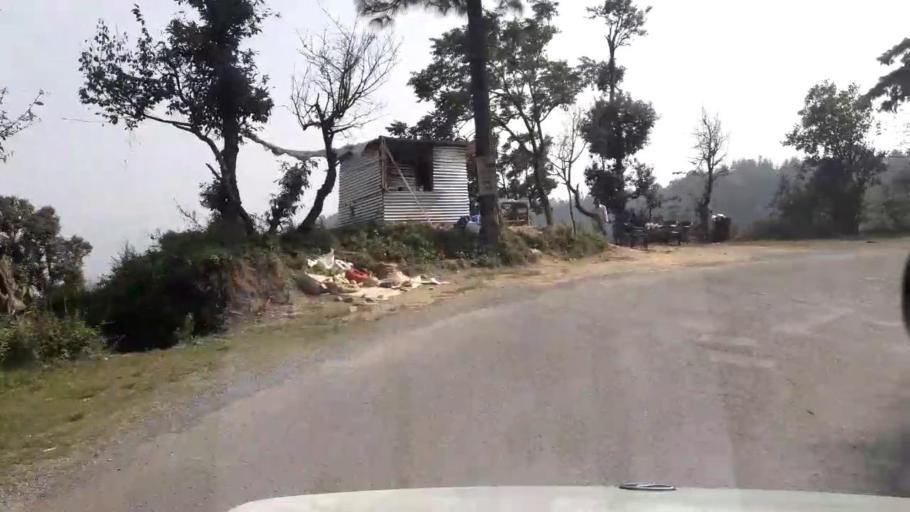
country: IN
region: Himachal Pradesh
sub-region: Shimla
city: Shimla
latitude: 31.0479
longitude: 77.1516
